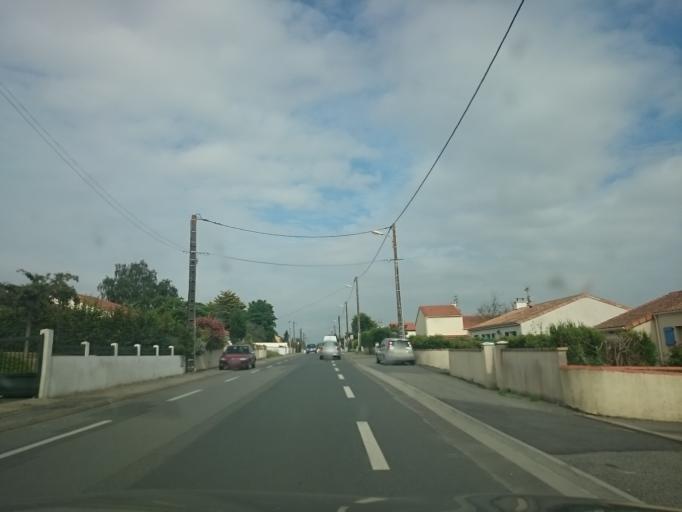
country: FR
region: Pays de la Loire
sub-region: Departement de la Loire-Atlantique
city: Le Pellerin
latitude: 47.2002
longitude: -1.7703
